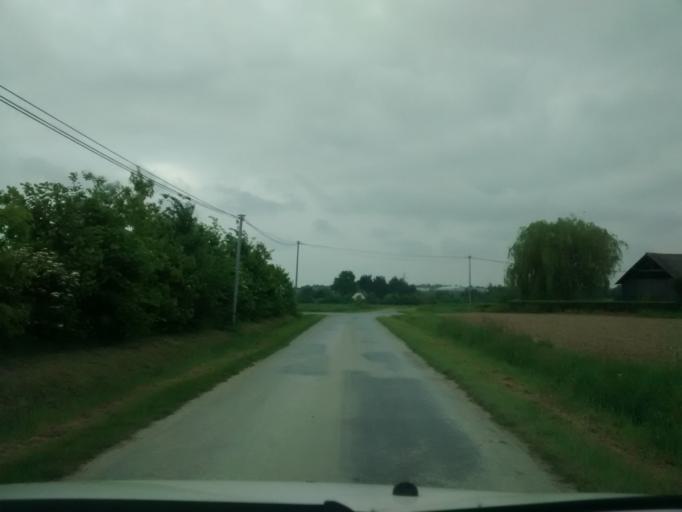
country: FR
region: Brittany
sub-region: Departement d'Ille-et-Vilaine
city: Cesson-Sevigne
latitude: 48.1272
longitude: -1.5784
